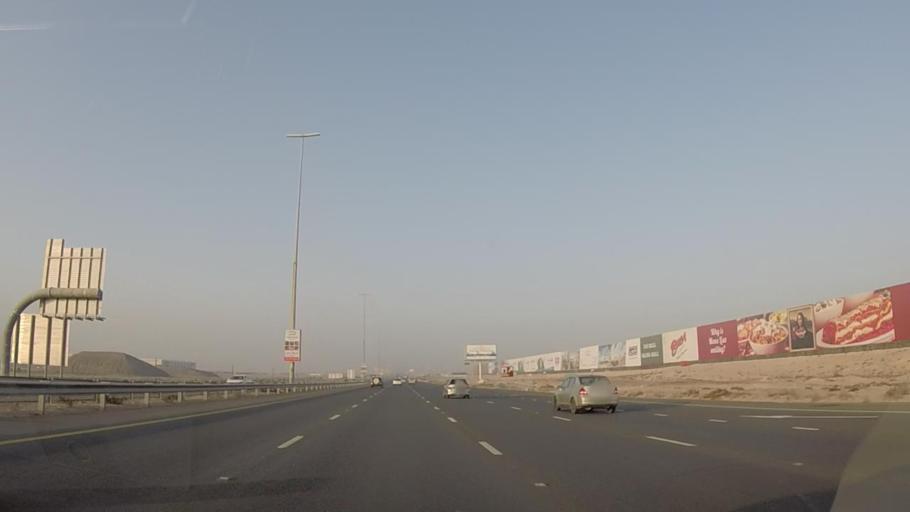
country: AE
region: Dubai
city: Dubai
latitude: 24.9435
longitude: 55.0519
